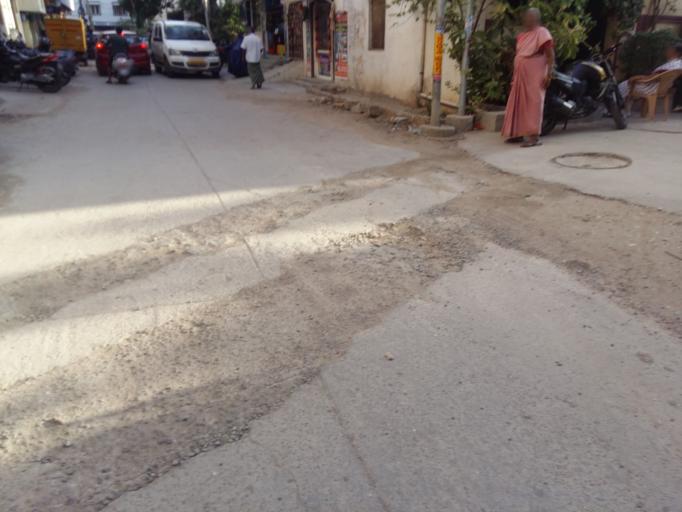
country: IN
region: Telangana
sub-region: Rangareddi
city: Kukatpalli
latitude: 17.4871
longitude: 78.3980
